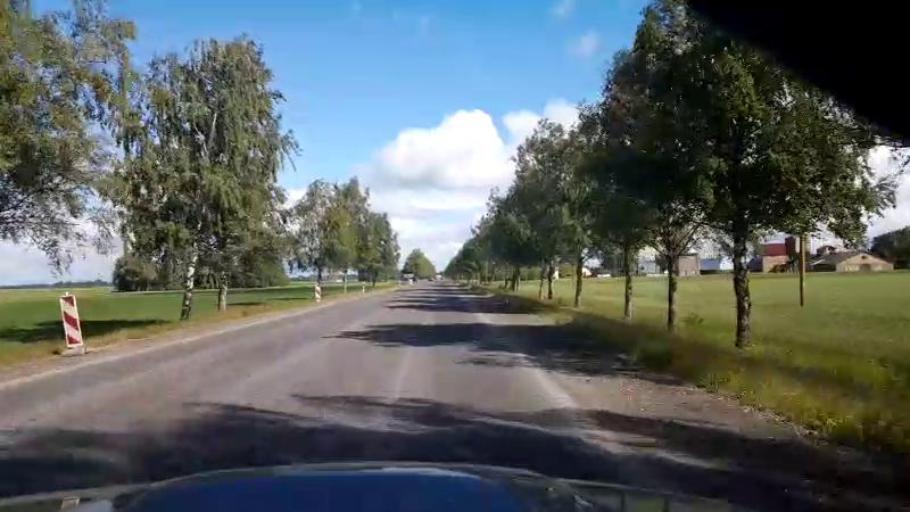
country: LV
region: Bauskas Rajons
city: Bauska
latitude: 56.3510
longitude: 24.2875
